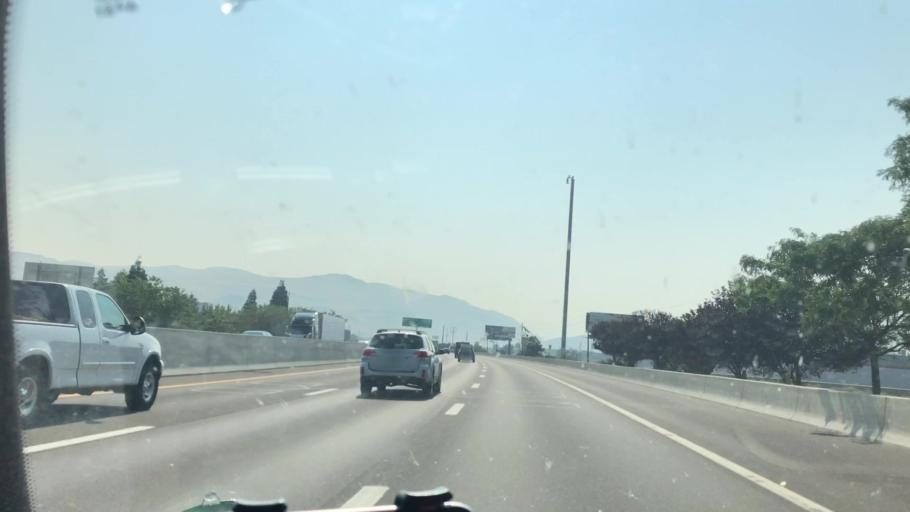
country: US
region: Nevada
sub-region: Washoe County
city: Sparks
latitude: 39.5298
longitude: -119.7302
